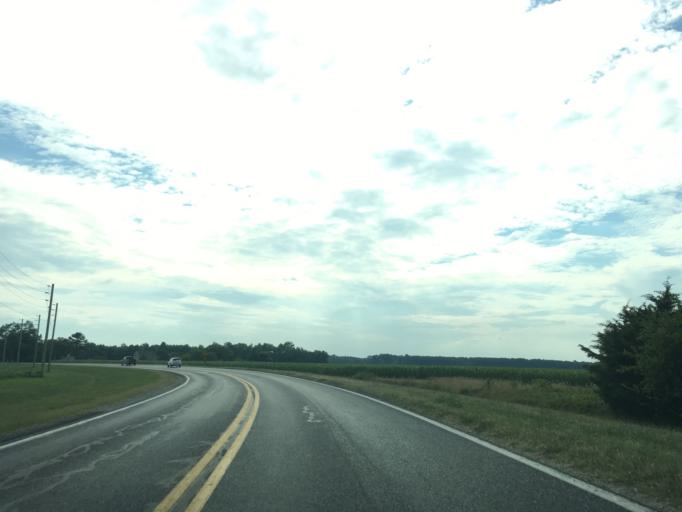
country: US
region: Delaware
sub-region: Sussex County
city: Bridgeville
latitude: 38.7636
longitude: -75.6119
